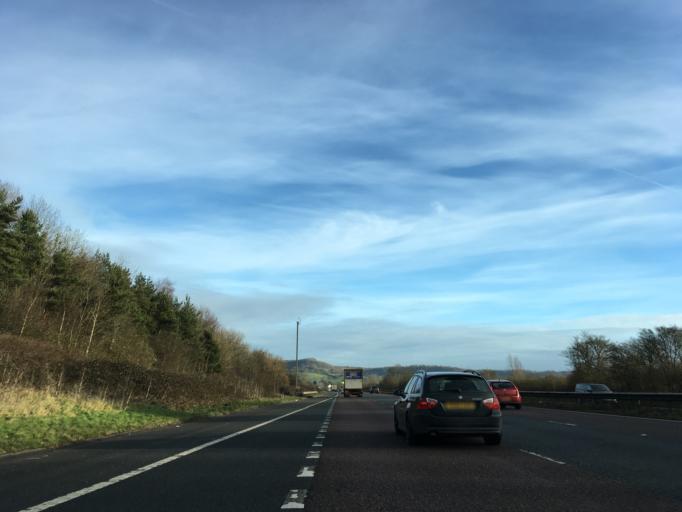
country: GB
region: England
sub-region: South Gloucestershire
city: Charfield
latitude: 51.6590
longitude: -2.4246
